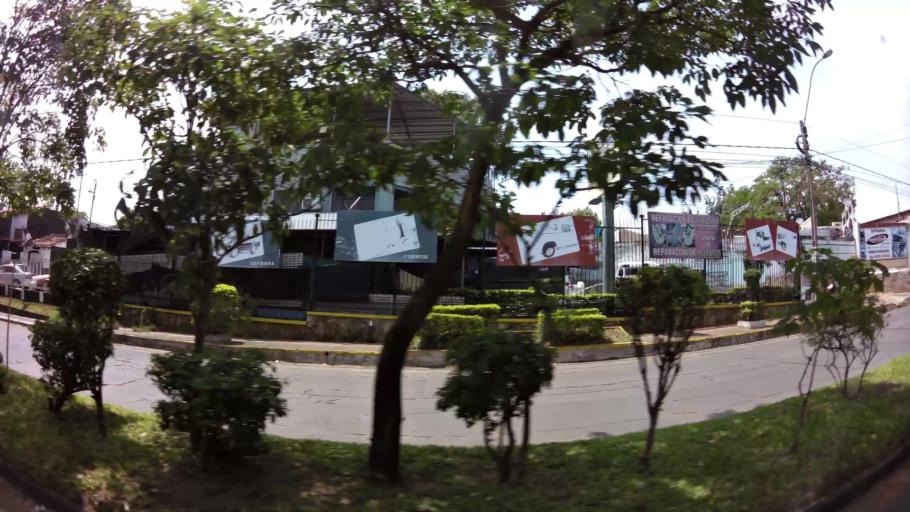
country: PY
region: Central
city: Lambare
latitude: -25.3179
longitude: -57.5990
